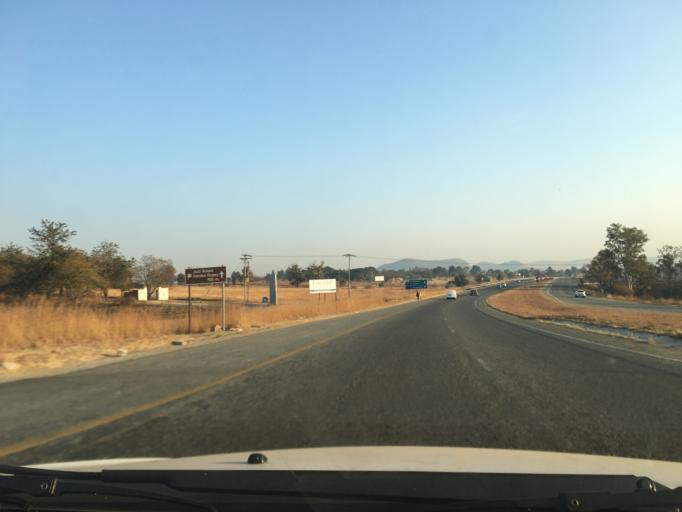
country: ZA
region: Gauteng
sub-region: West Rand District Municipality
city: Muldersdriseloop
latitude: -26.0242
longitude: 27.8623
